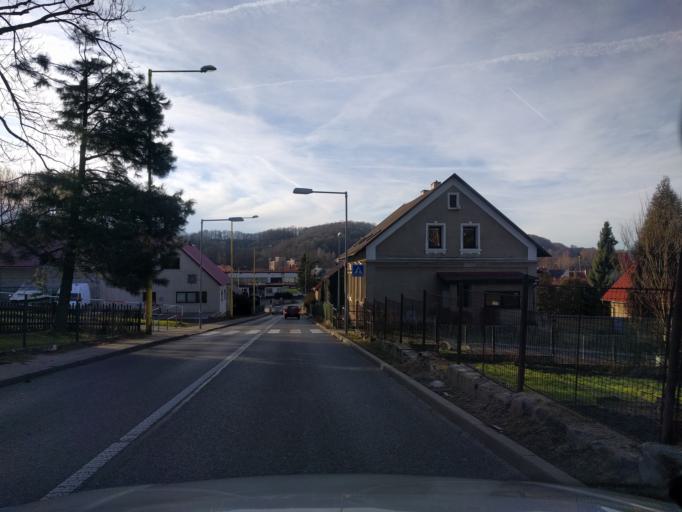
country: CZ
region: Liberecky
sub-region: Okres Liberec
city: Frydlant
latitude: 50.9217
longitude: 15.0854
